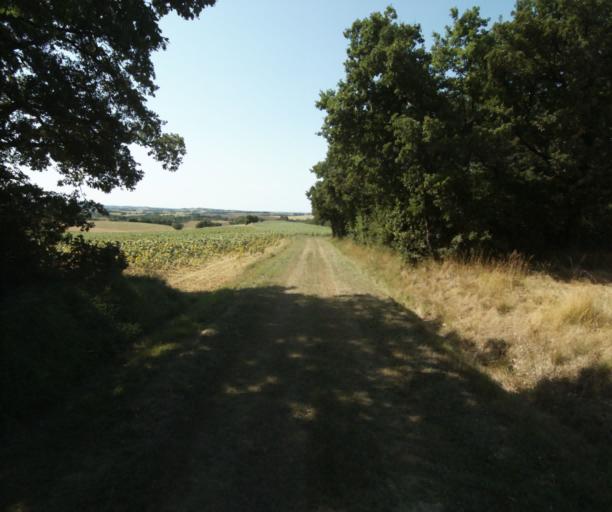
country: FR
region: Midi-Pyrenees
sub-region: Departement de la Haute-Garonne
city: Saint-Felix-Lauragais
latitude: 43.4401
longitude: 1.8427
